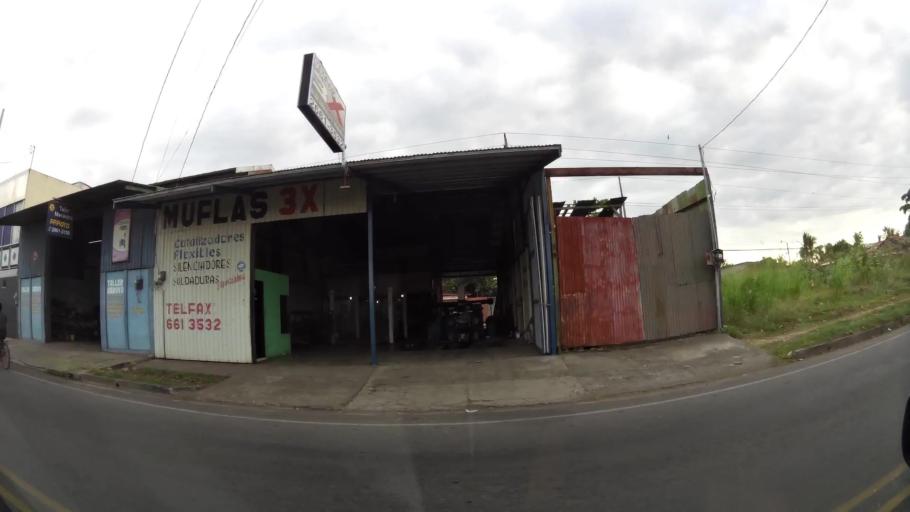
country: CR
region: Puntarenas
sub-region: Canton Central de Puntarenas
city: Puntarenas
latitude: 9.9791
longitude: -84.8213
